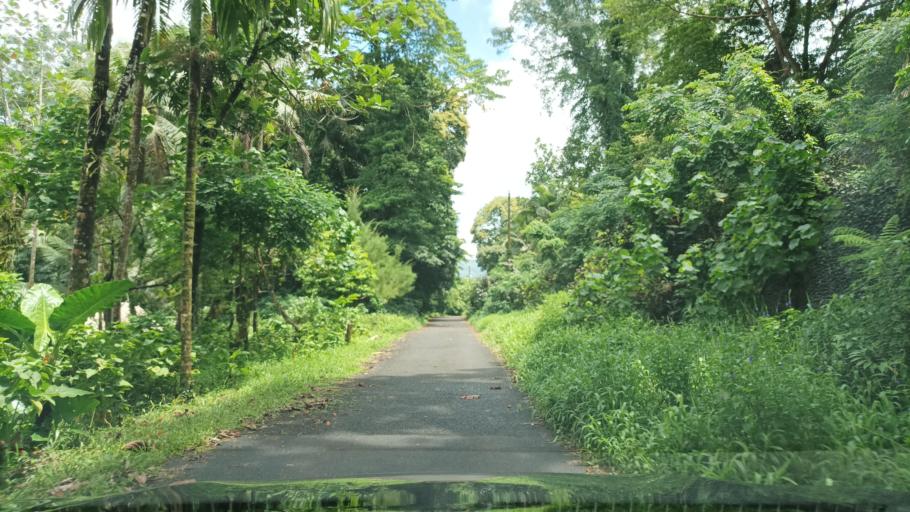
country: FM
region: Pohnpei
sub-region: Kolonia Municipality
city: Kolonia
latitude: 6.9626
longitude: 158.2231
